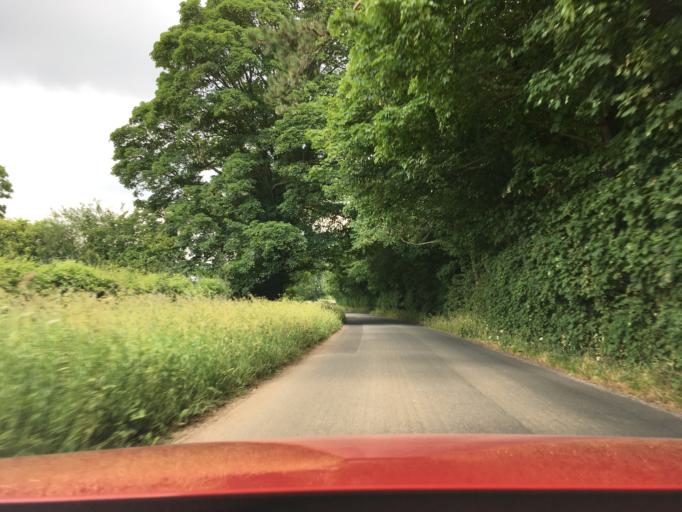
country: GB
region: England
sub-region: Gloucestershire
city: Coates
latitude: 51.7288
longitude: -2.0636
